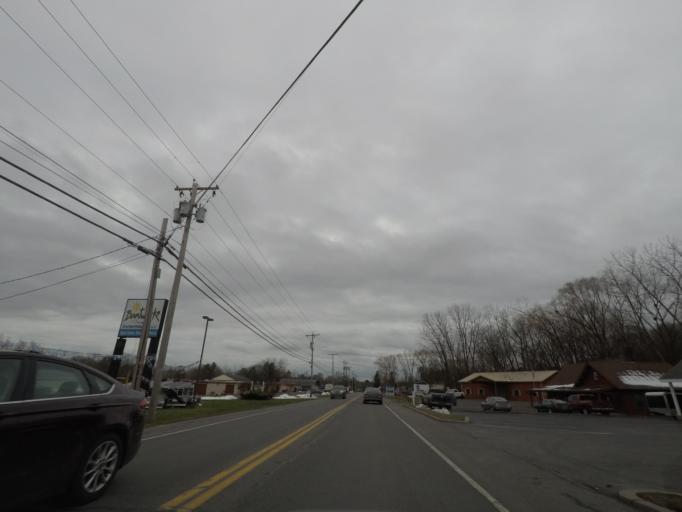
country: US
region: New York
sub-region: Schenectady County
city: East Glenville
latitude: 42.9042
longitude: -73.9034
